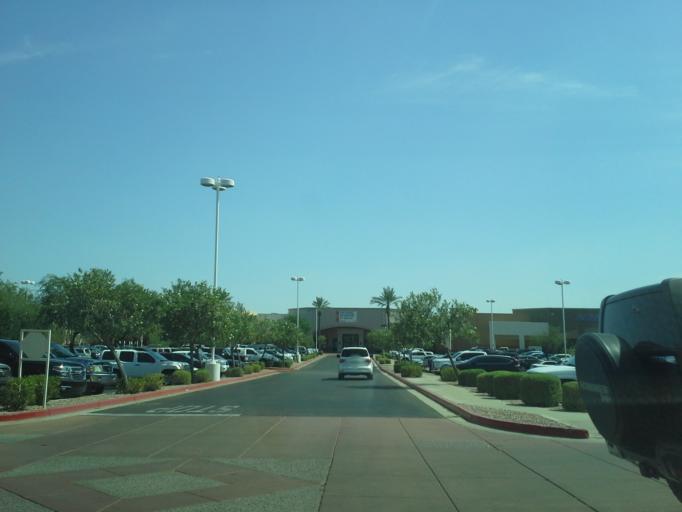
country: US
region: Arizona
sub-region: Maricopa County
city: Guadalupe
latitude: 33.3189
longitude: -111.9782
